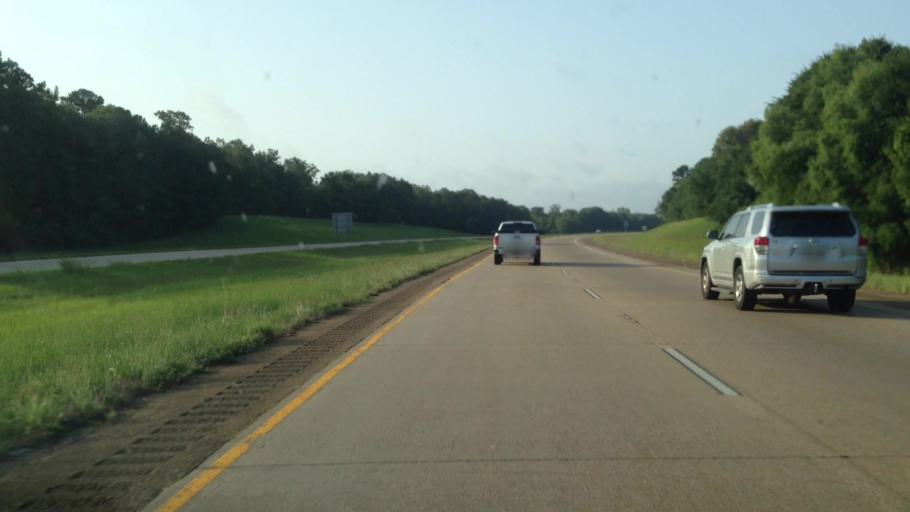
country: US
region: Louisiana
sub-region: Rapides Parish
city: Woodworth
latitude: 31.1567
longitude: -92.4556
